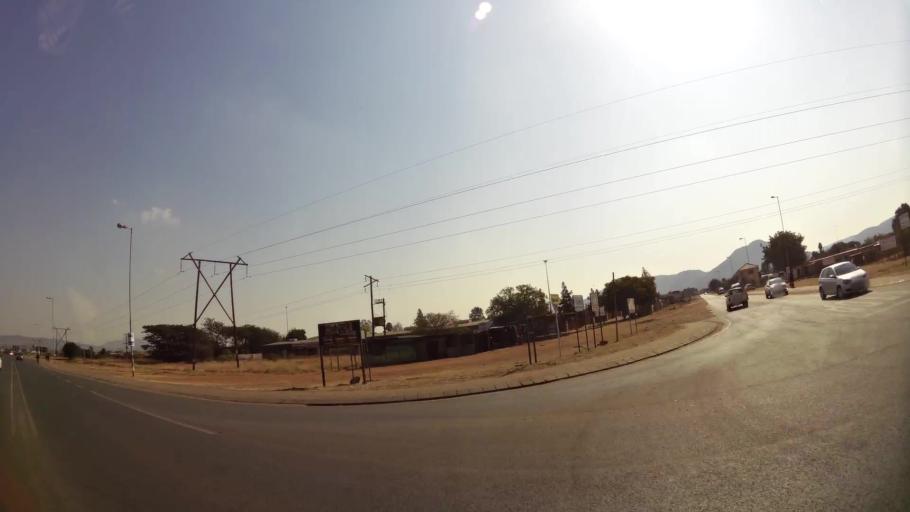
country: ZA
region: North-West
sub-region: Bojanala Platinum District Municipality
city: Mogwase
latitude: -25.3755
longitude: 27.0649
